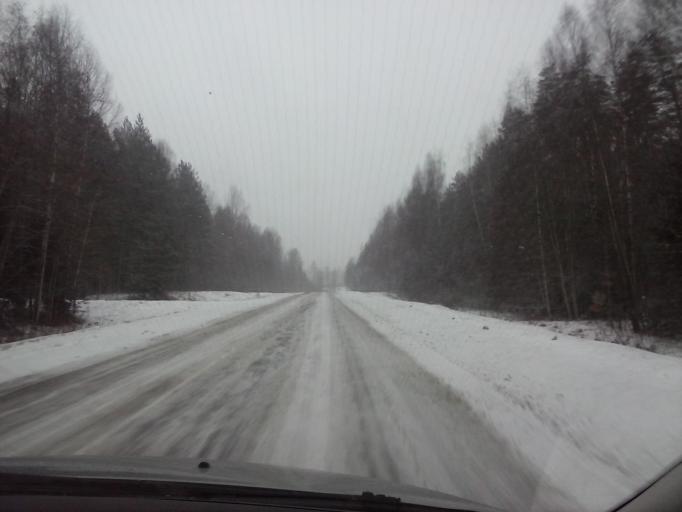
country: LV
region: Valkas Rajons
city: Valka
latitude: 57.7199
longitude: 25.9340
